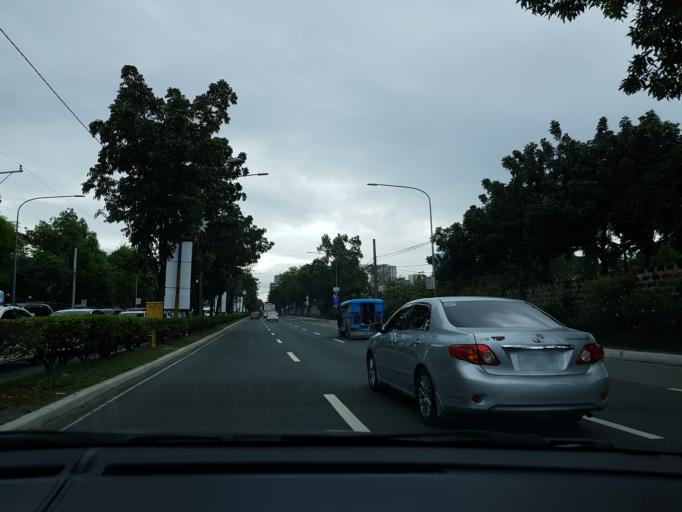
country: PH
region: Metro Manila
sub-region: Pasig
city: Pasig City
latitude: 14.5993
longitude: 121.0504
